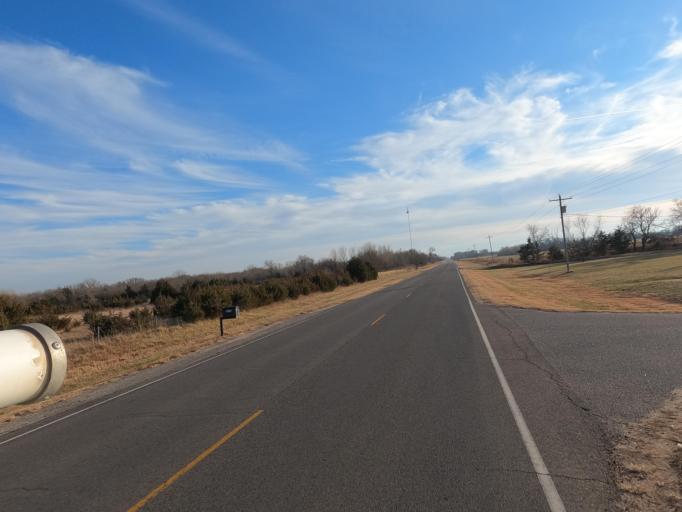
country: US
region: Kansas
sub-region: Reno County
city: Buhler
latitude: 38.1056
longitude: -97.7756
